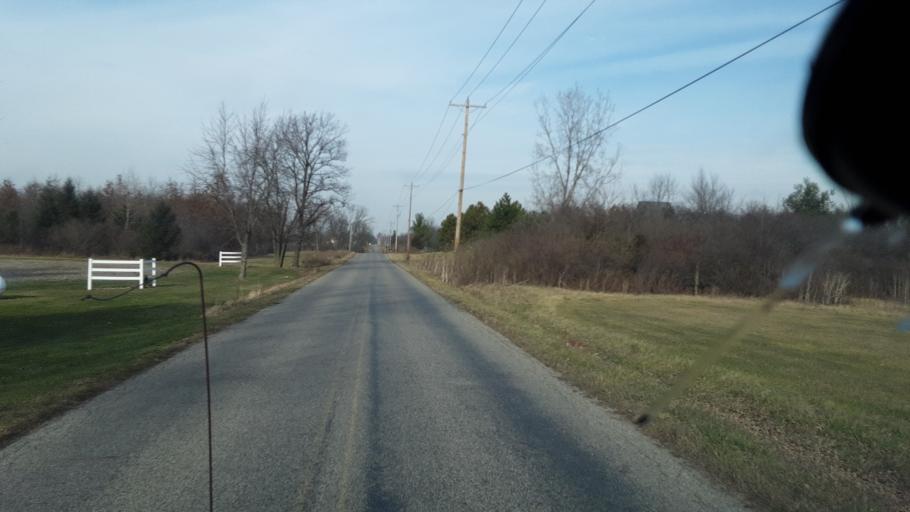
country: US
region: Indiana
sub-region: DeKalb County
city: Butler
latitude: 41.3921
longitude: -84.8891
